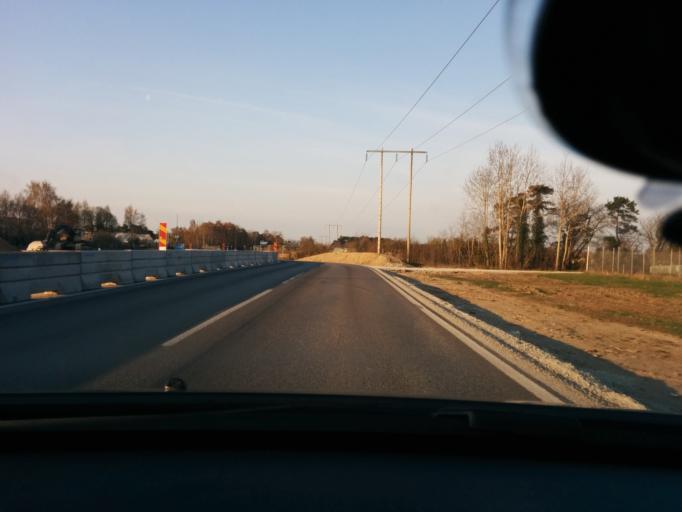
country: SE
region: Gotland
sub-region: Gotland
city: Visby
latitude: 57.6217
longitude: 18.3186
